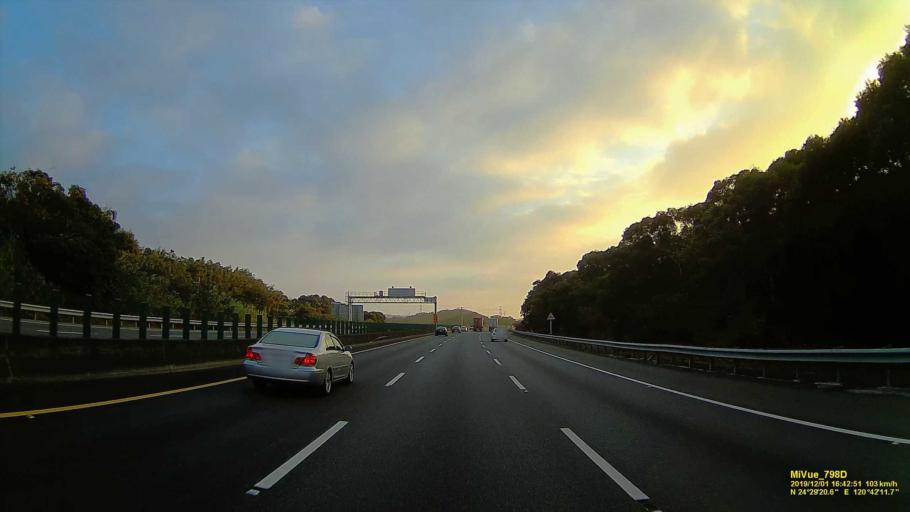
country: TW
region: Taiwan
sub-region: Miaoli
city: Miaoli
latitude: 24.4891
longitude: 120.7037
